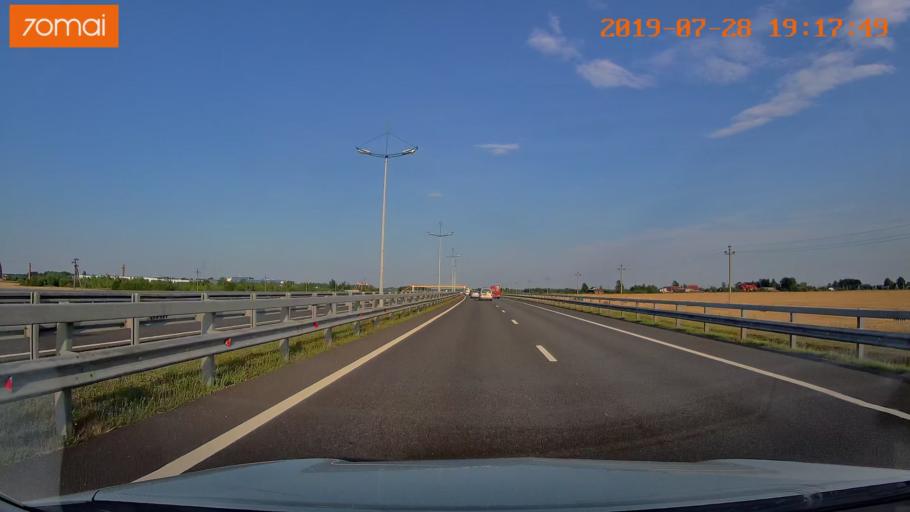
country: RU
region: Kaliningrad
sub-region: Zelenogradskiy Rayon
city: Zelenogradsk
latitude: 54.9201
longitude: 20.4135
